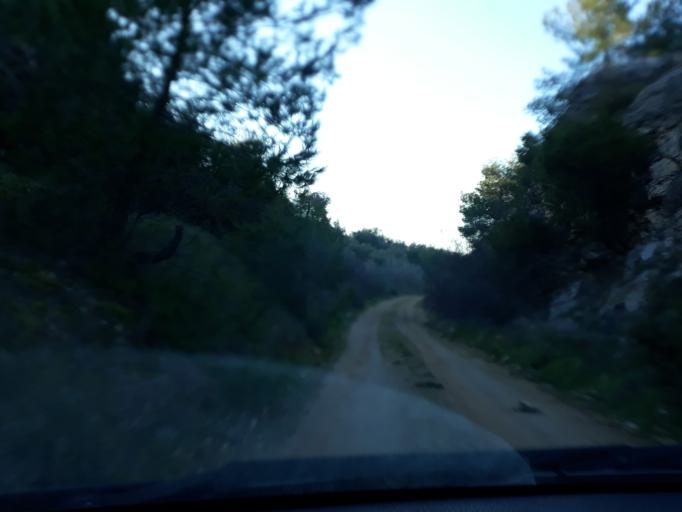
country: GR
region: Central Greece
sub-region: Nomos Voiotias
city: Asopia
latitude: 38.2734
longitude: 23.5310
